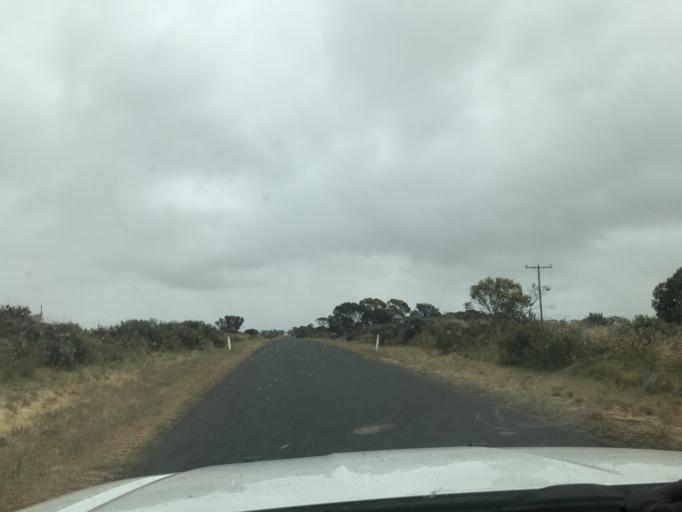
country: AU
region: South Australia
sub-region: Tatiara
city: Bordertown
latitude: -36.1166
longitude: 141.0330
